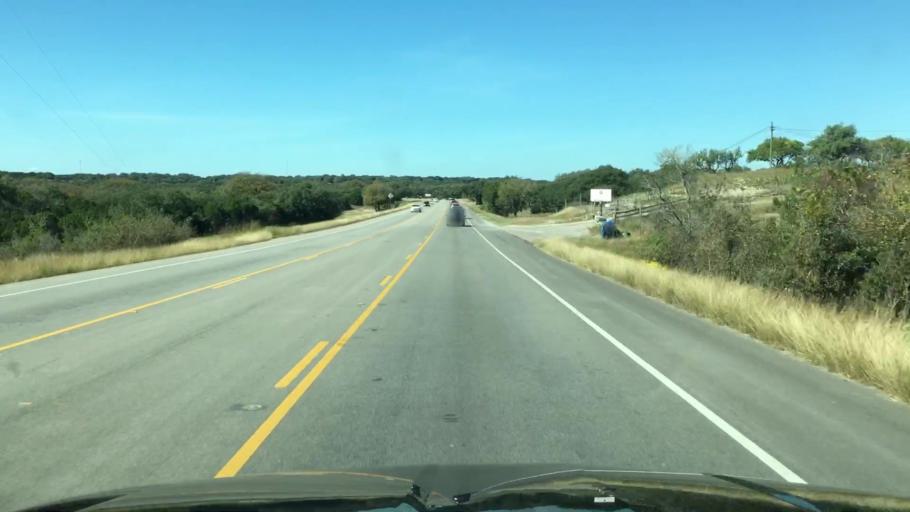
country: US
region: Texas
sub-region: Hays County
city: Dripping Springs
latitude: 30.2003
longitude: -98.1897
